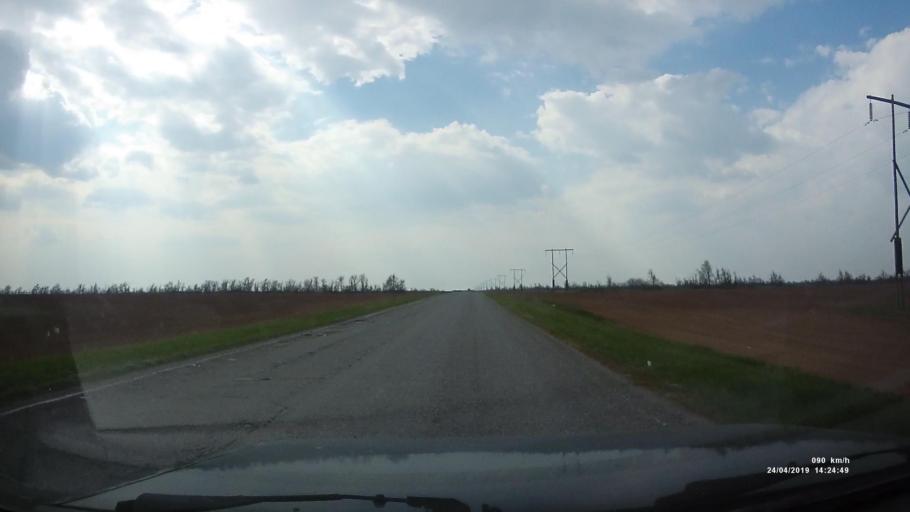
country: RU
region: Kalmykiya
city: Arshan'
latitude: 46.3291
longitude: 44.0903
